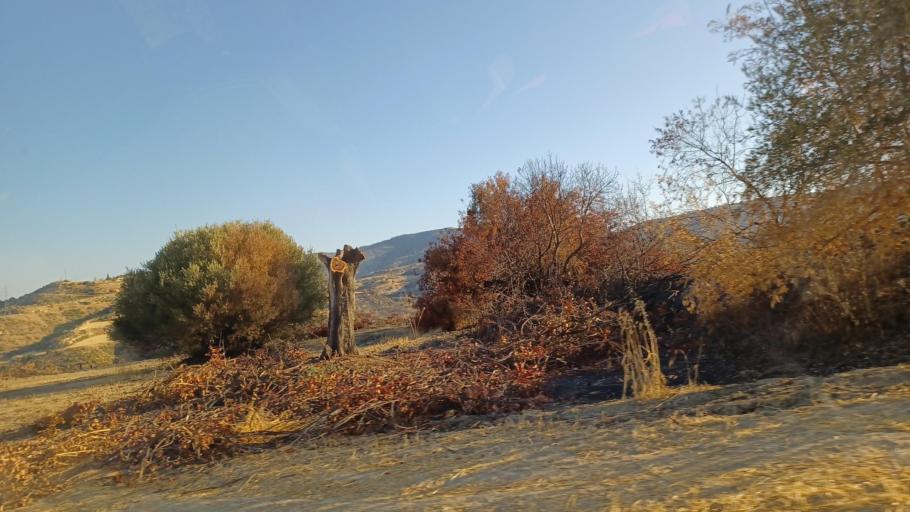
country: CY
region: Pafos
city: Polis
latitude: 34.9766
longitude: 32.4570
